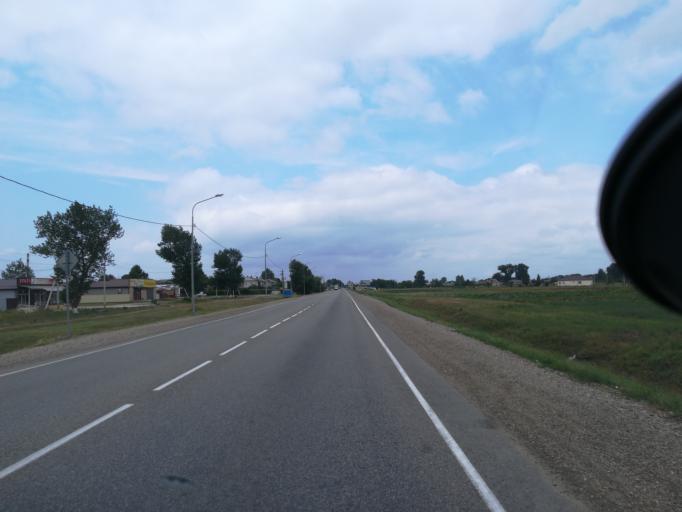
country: RU
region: Krasnodarskiy
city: Korzhevskiy
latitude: 45.1964
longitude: 37.6703
